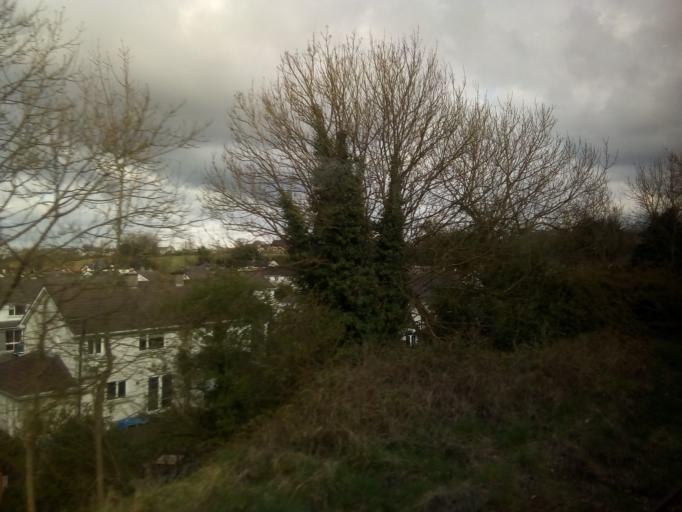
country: IE
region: Leinster
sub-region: An Iarmhi
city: An Muileann gCearr
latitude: 53.5212
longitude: -7.3359
